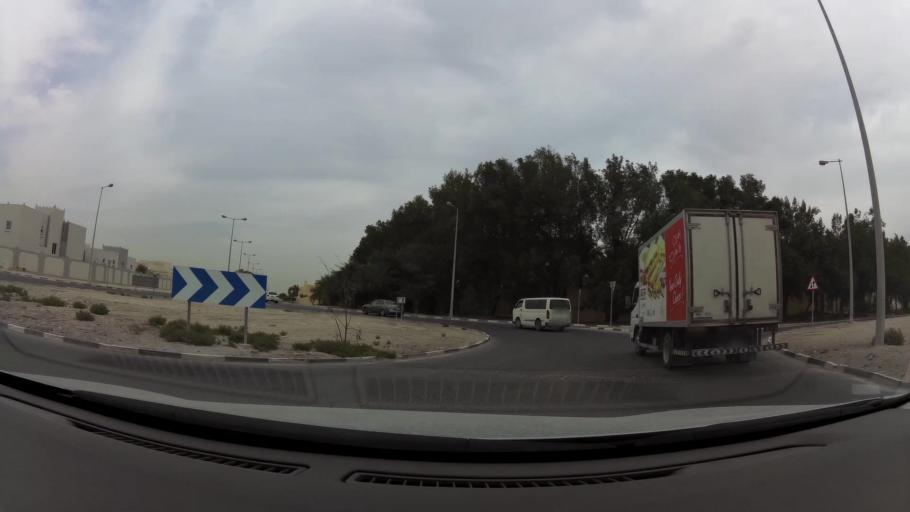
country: QA
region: Baladiyat ar Rayyan
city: Ar Rayyan
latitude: 25.2315
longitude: 51.4648
